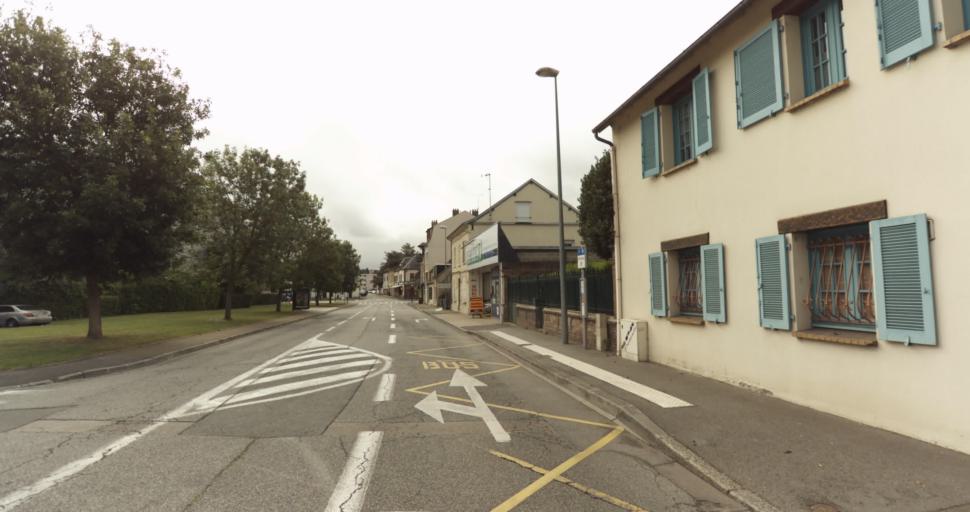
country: FR
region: Haute-Normandie
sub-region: Departement de l'Eure
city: Evreux
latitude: 49.0284
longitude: 1.1432
